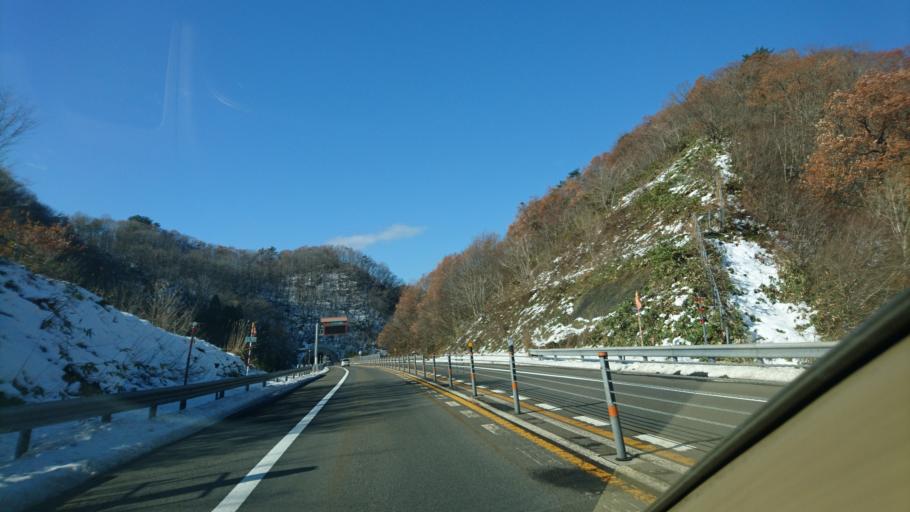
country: JP
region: Akita
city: Yokotemachi
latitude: 39.3143
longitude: 140.7695
